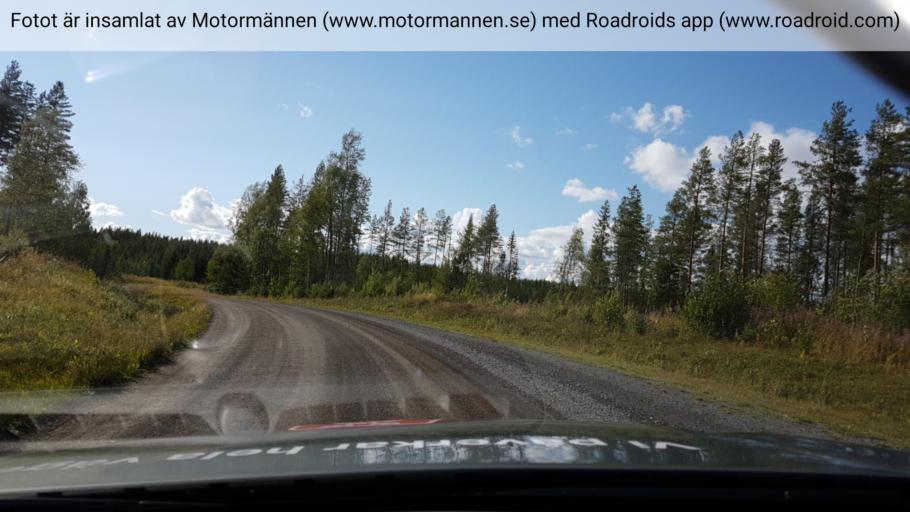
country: SE
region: Jaemtland
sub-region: OEstersunds Kommun
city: Lit
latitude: 63.3231
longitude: 15.2136
